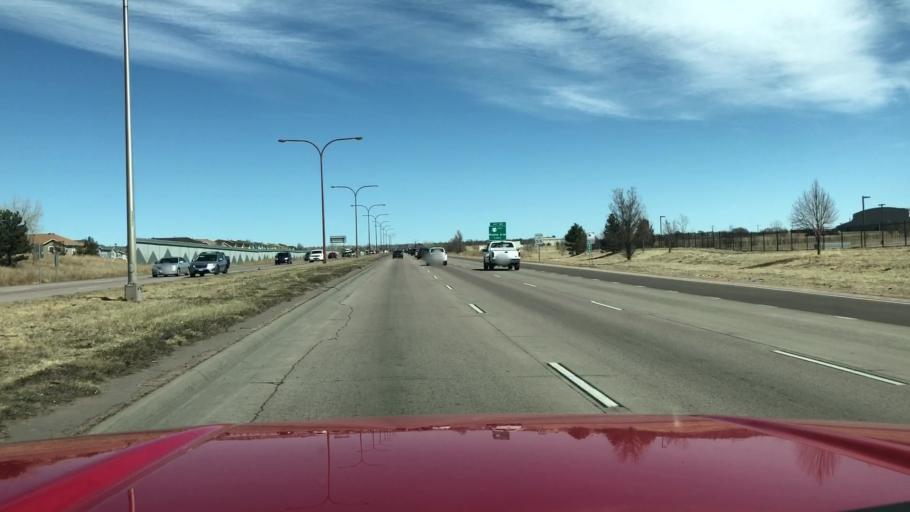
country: US
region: Colorado
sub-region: El Paso County
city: Cimarron Hills
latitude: 38.8176
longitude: -104.7290
